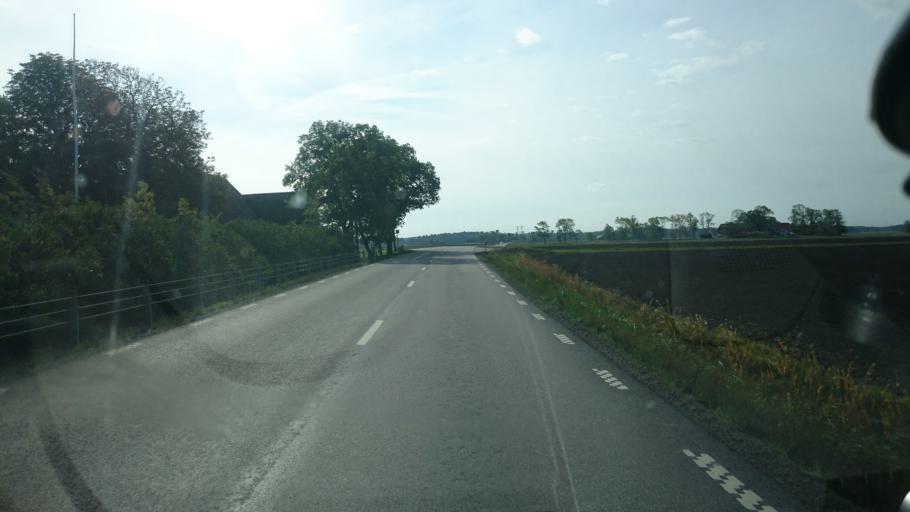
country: SE
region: Vaestra Goetaland
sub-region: Vanersborgs Kommun
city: Vargon
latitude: 58.2774
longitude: 12.3986
